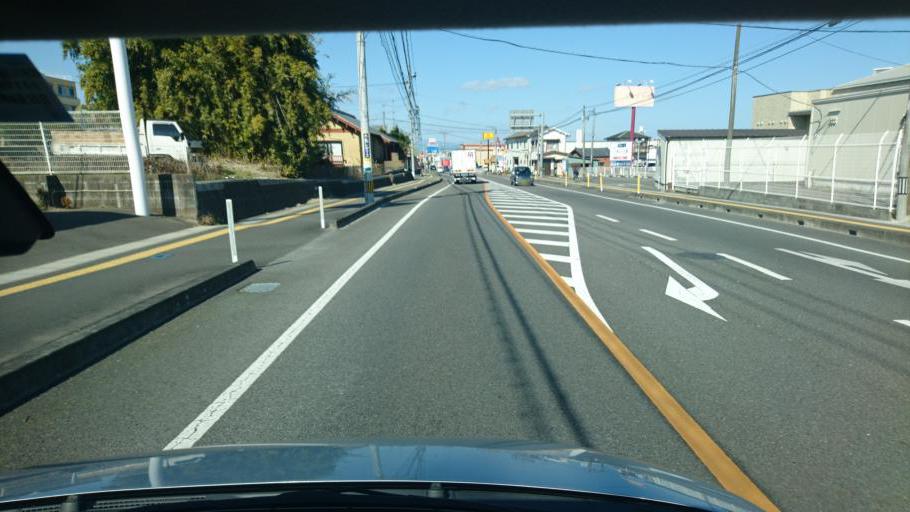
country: JP
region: Miyazaki
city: Miyazaki-shi
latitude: 31.8698
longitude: 131.4317
